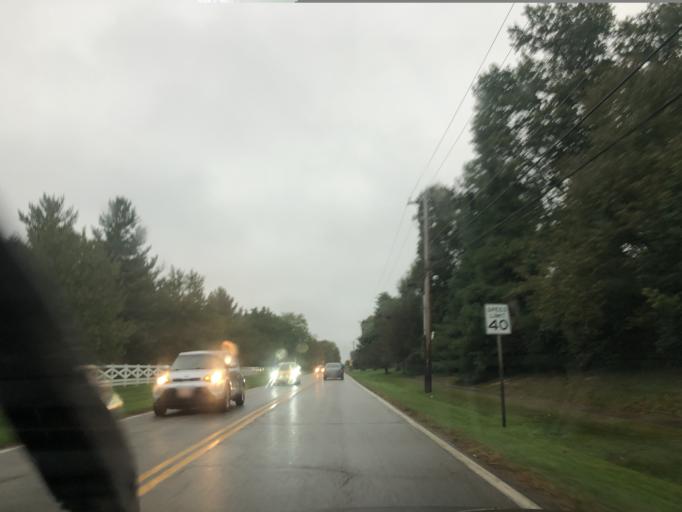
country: US
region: Ohio
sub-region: Clermont County
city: Mulberry
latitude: 39.2170
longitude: -84.2431
